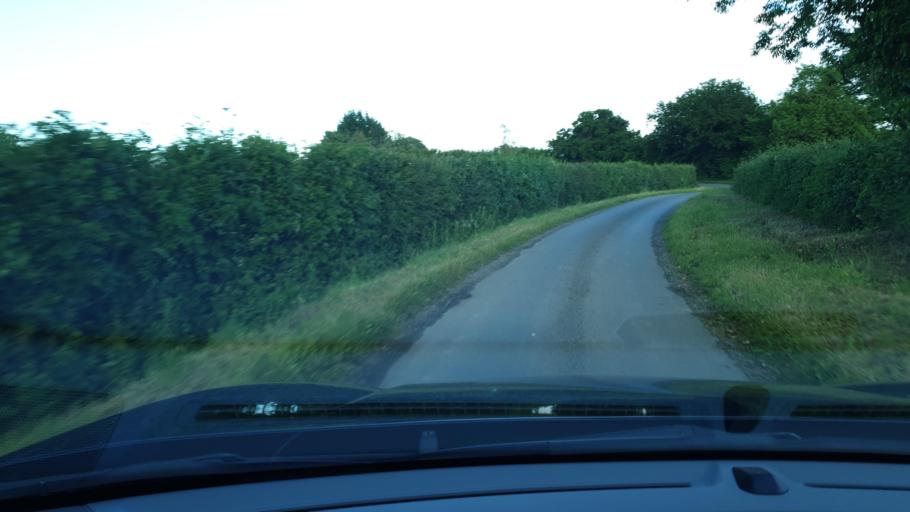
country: IE
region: Leinster
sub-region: An Mhi
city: Ashbourne
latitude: 53.4768
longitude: -6.3430
